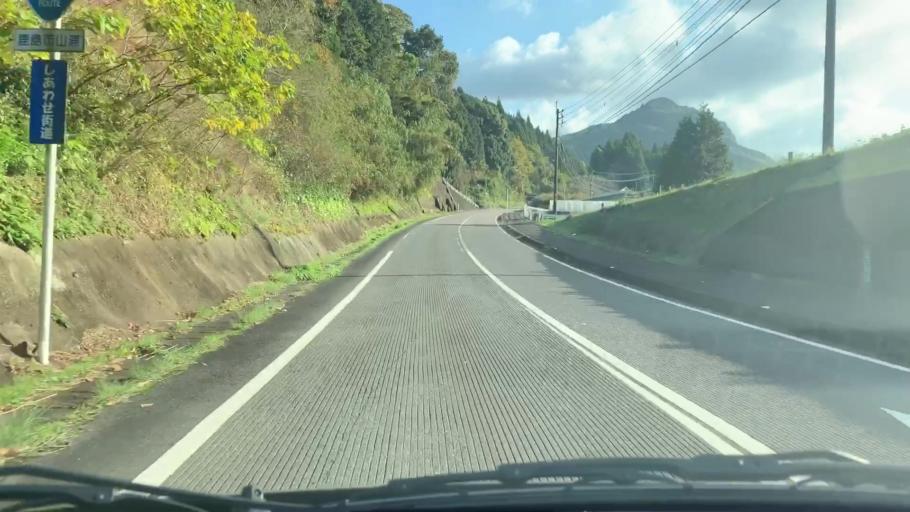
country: JP
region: Saga Prefecture
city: Kashima
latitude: 33.0566
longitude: 130.0711
